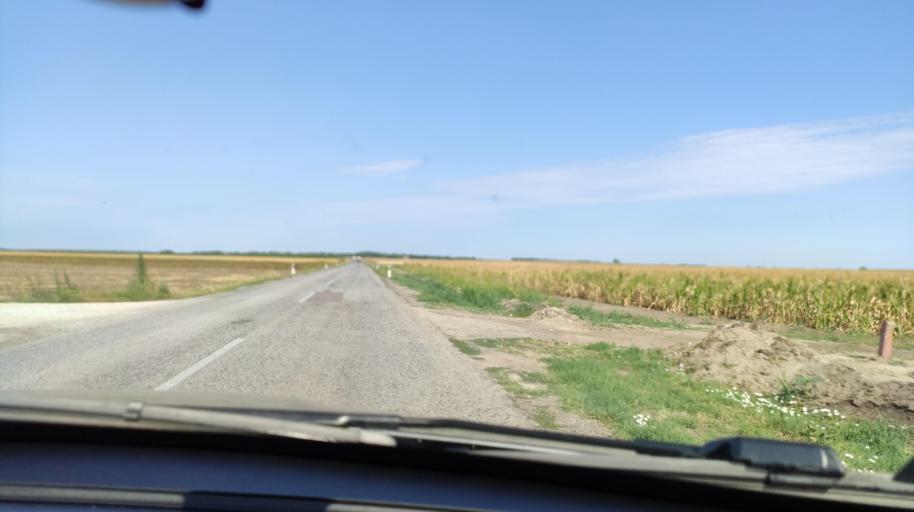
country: RS
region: Autonomna Pokrajina Vojvodina
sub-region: Severnobacki Okrug
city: Backa Topola
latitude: 45.8408
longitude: 19.5687
